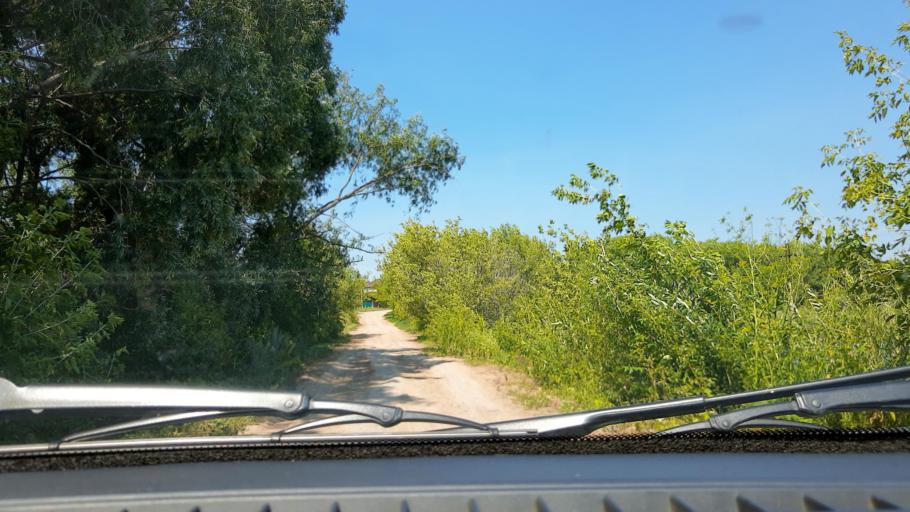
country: RU
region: Bashkortostan
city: Kushnarenkovo
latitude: 55.0681
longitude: 55.1644
